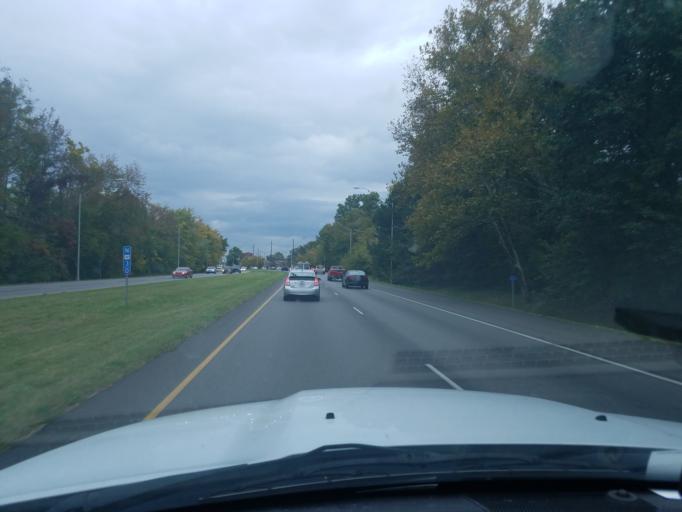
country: US
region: Indiana
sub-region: Vanderburgh County
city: Evansville
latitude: 37.9654
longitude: -87.5428
